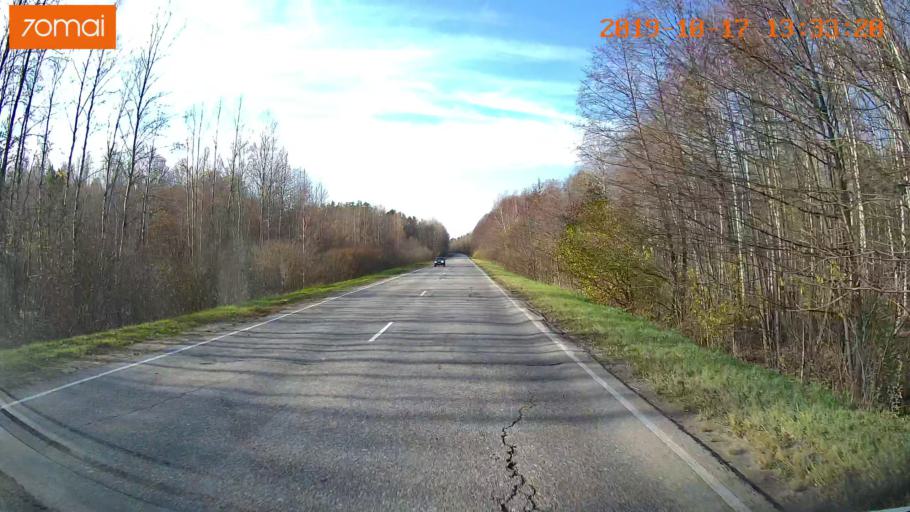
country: RU
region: Vladimir
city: Velikodvorskiy
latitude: 55.1419
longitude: 40.7439
